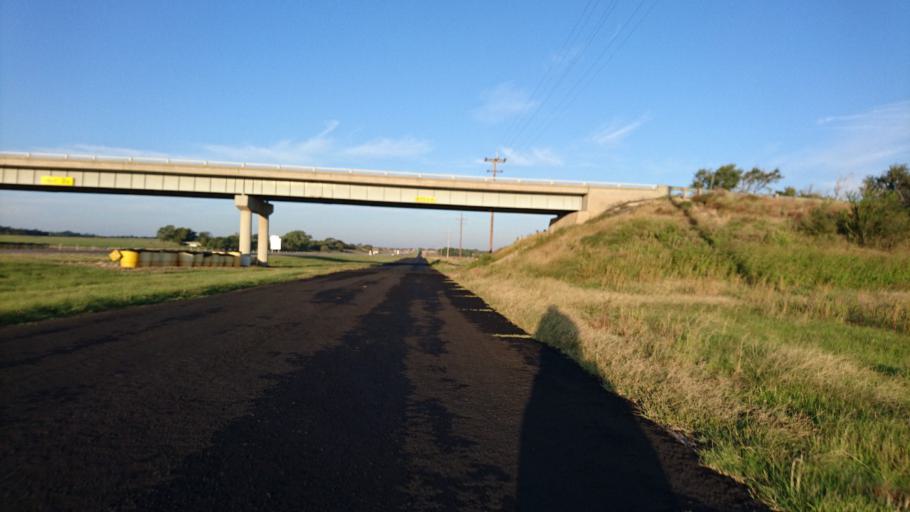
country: US
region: Oklahoma
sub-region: Beckham County
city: Sayre
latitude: 35.2624
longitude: -99.6816
